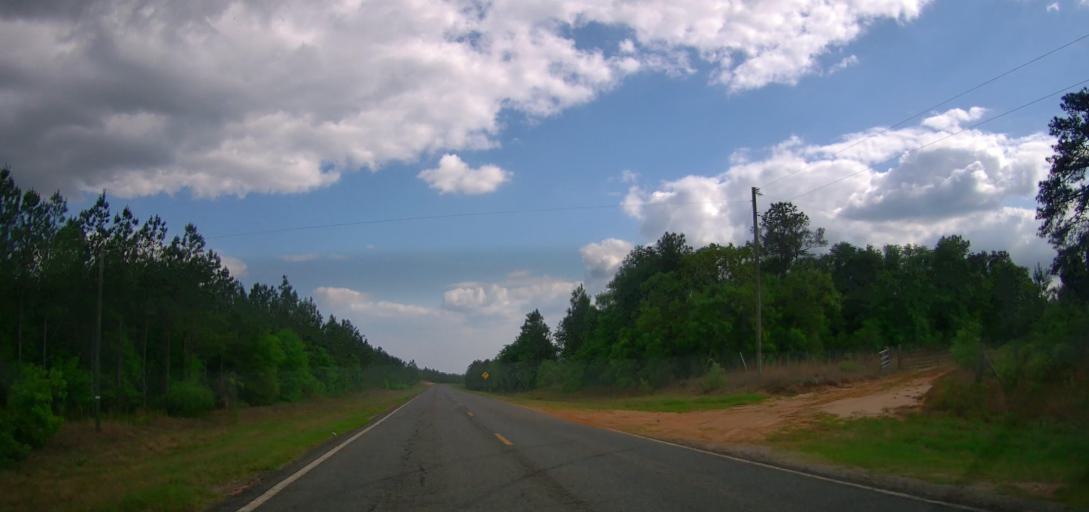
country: US
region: Georgia
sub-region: Johnson County
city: Wrightsville
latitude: 32.7568
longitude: -82.9283
